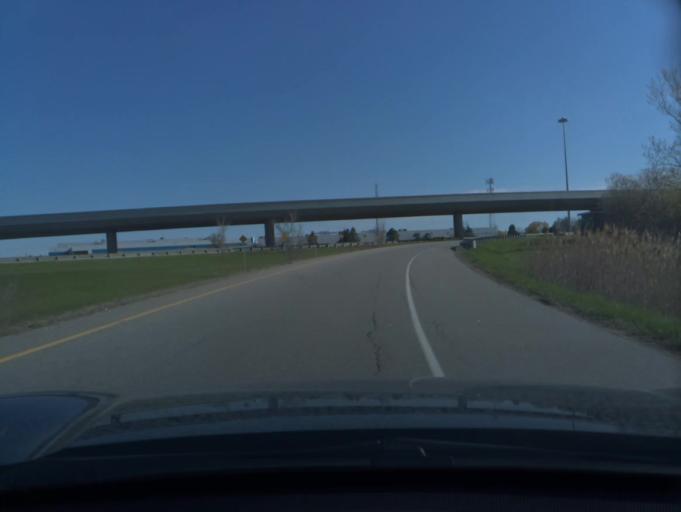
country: CA
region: Ontario
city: North Perth
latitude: 43.8043
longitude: -80.9998
